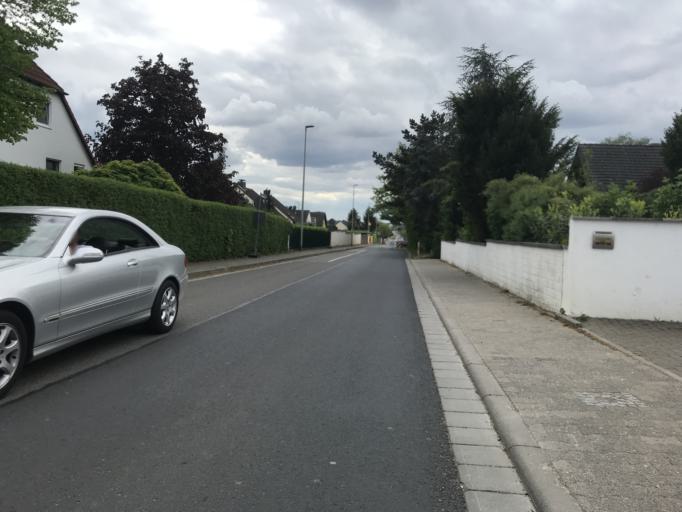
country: DE
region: Rheinland-Pfalz
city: Lorzweiler
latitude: 49.8972
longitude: 8.2935
